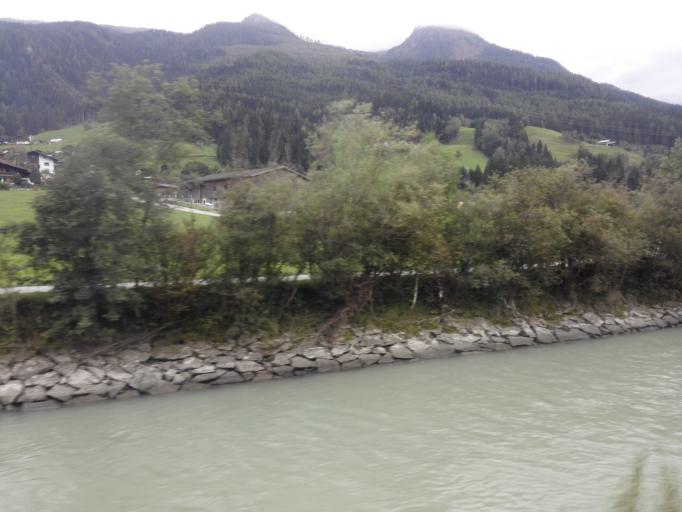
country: AT
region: Salzburg
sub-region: Politischer Bezirk Zell am See
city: Bramberg am Wildkogel
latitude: 47.2725
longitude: 12.3550
